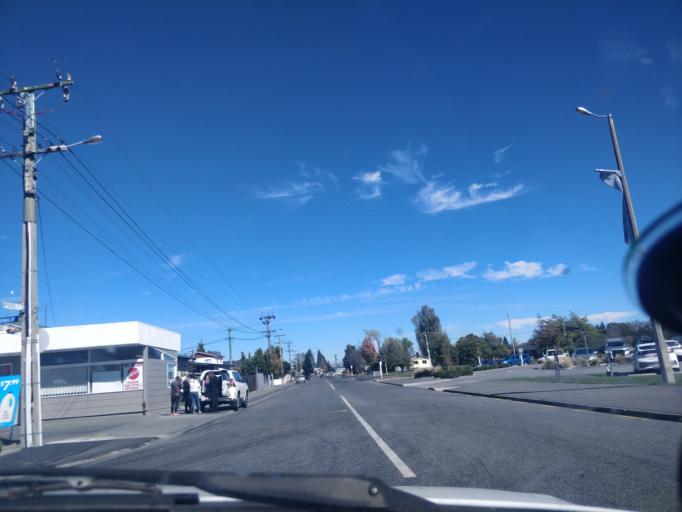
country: NZ
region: Canterbury
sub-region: Timaru District
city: Pleasant Point
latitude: -44.2577
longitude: 170.1000
